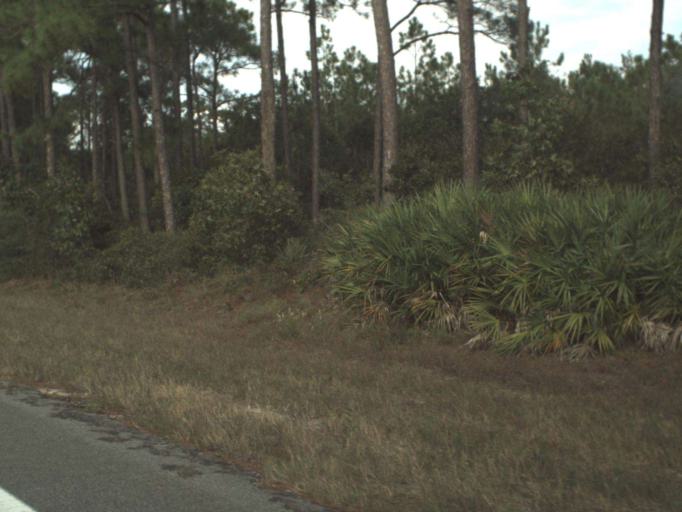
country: US
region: Florida
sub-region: Franklin County
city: Carrabelle
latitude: 29.9224
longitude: -84.5204
